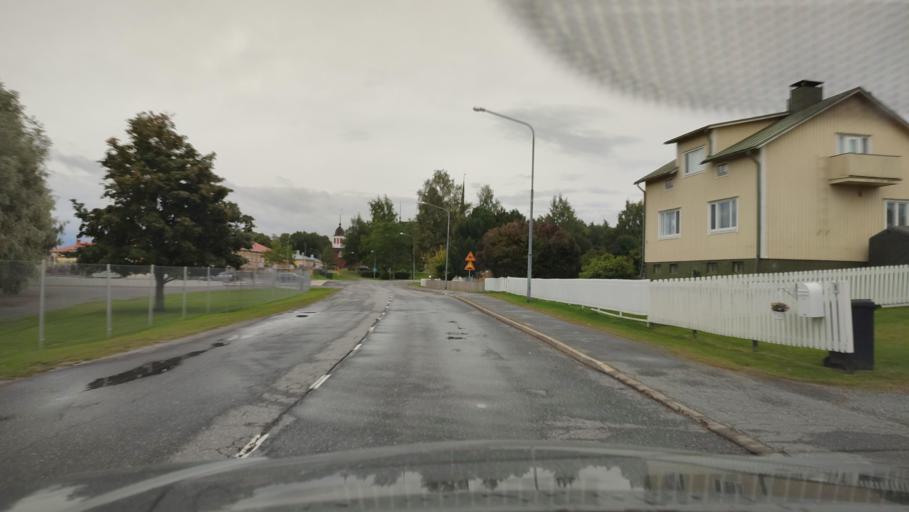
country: FI
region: Ostrobothnia
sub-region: Sydosterbotten
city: Kristinestad
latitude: 62.2774
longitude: 21.3727
